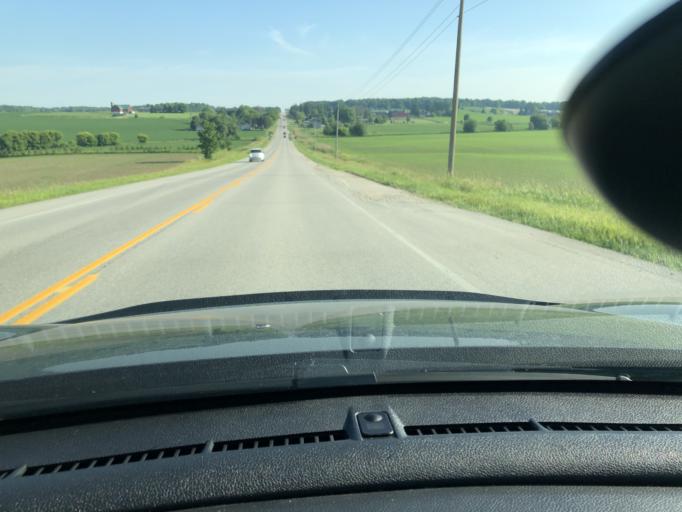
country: CA
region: Ontario
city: Stratford
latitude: 43.4184
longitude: -80.8380
